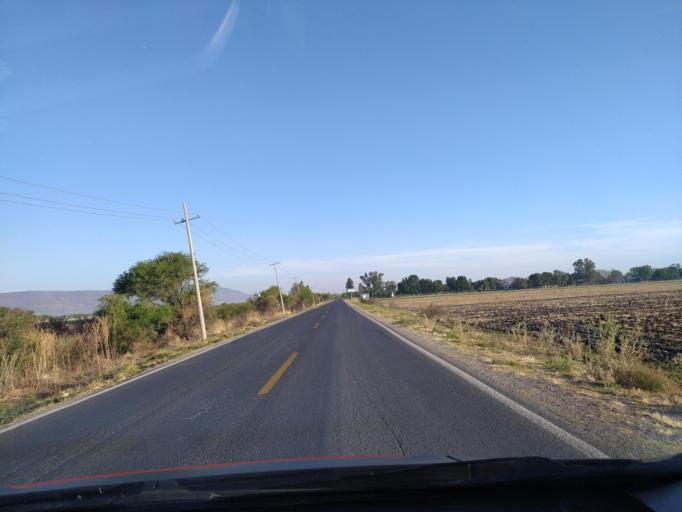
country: MX
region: Guanajuato
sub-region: San Francisco del Rincon
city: San Ignacio de Hidalgo
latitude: 20.9344
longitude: -101.8534
